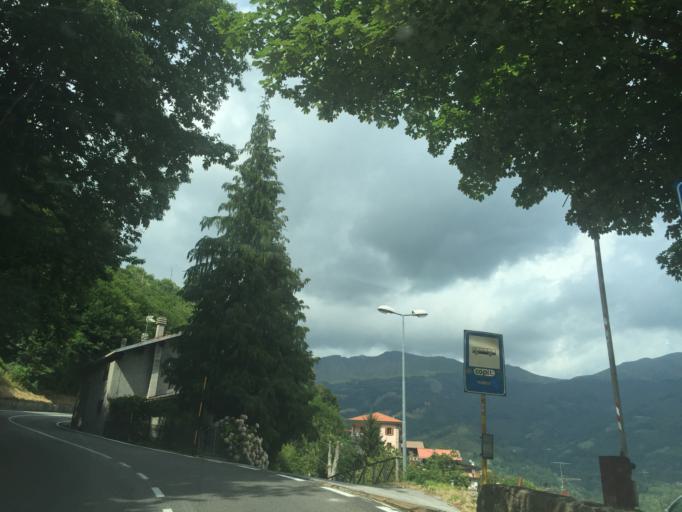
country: IT
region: Tuscany
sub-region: Provincia di Pistoia
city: Cutigliano
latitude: 44.1203
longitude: 10.7263
